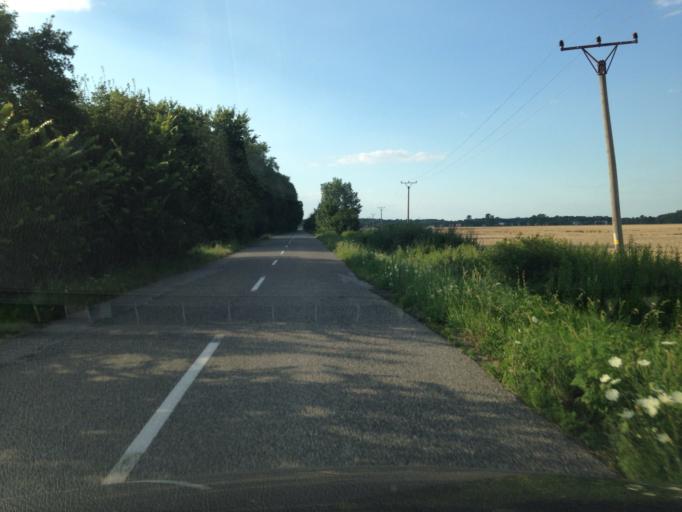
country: AT
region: Lower Austria
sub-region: Politischer Bezirk Ganserndorf
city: Angern an der March
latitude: 48.3938
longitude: 16.8636
